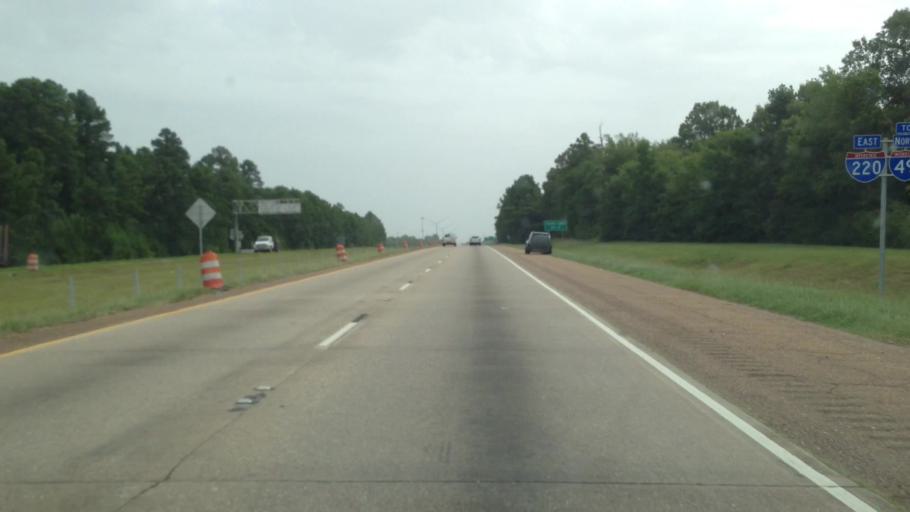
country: US
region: Louisiana
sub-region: Caddo Parish
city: Shreveport
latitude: 32.4790
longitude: -93.8329
